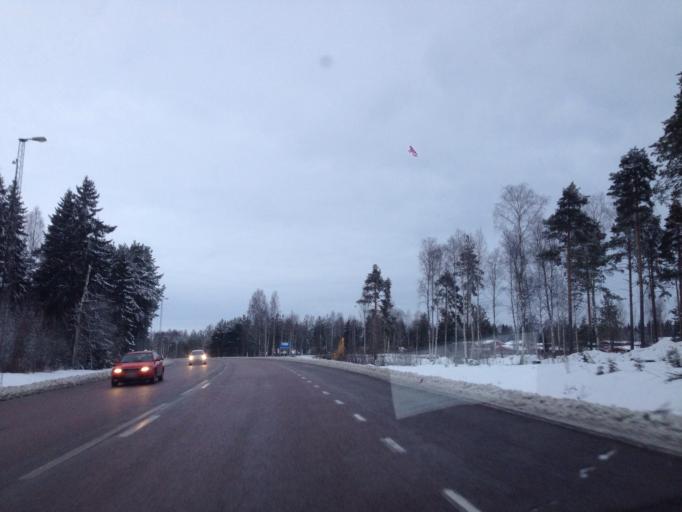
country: SE
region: Dalarna
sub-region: Mora Kommun
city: Mora
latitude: 61.0116
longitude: 14.5905
